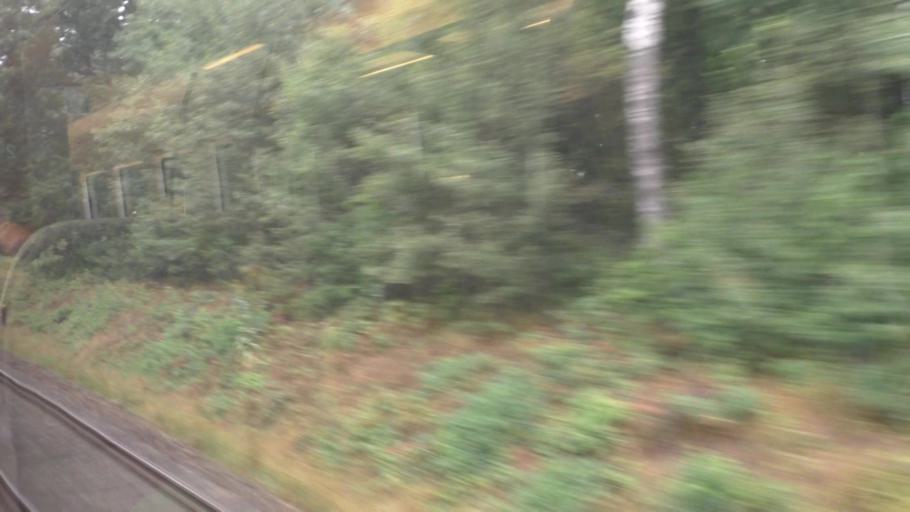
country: DE
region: Saxony
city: Arnsdorf
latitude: 51.0978
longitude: 13.9671
